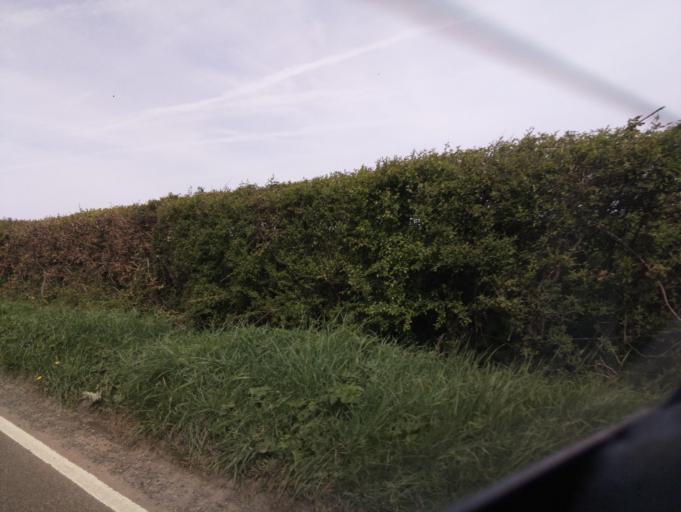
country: GB
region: England
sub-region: Somerset
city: Street
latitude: 51.1160
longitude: -2.7786
